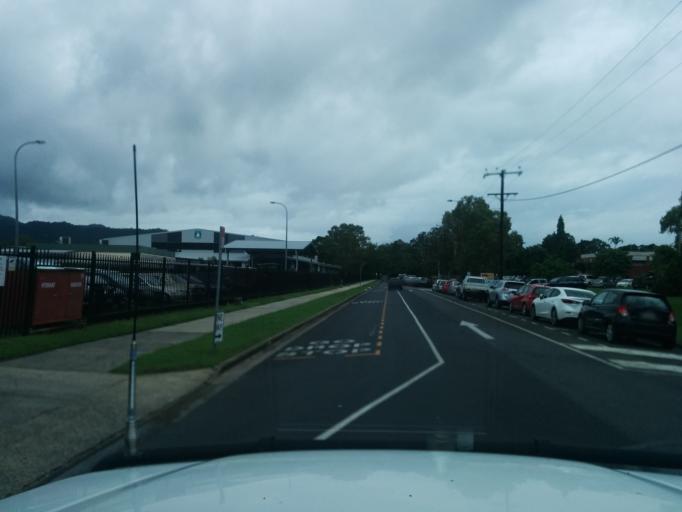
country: AU
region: Queensland
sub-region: Cairns
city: Cairns
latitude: -16.9223
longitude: 145.7536
